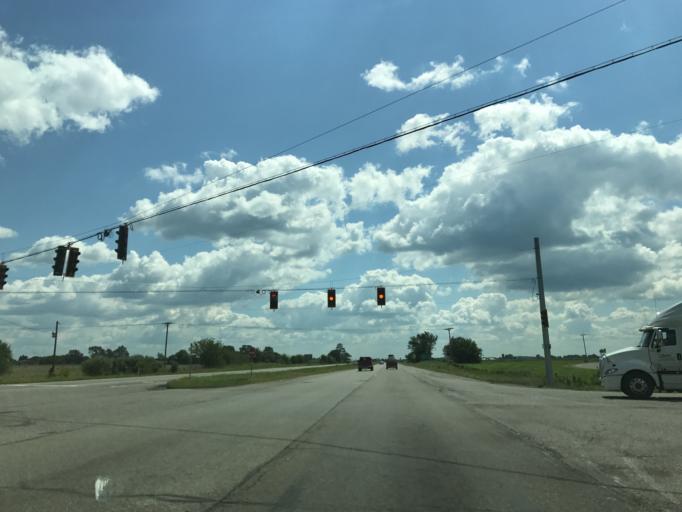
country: US
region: Indiana
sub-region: Marshall County
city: Plymouth
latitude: 41.3425
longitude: -86.2631
